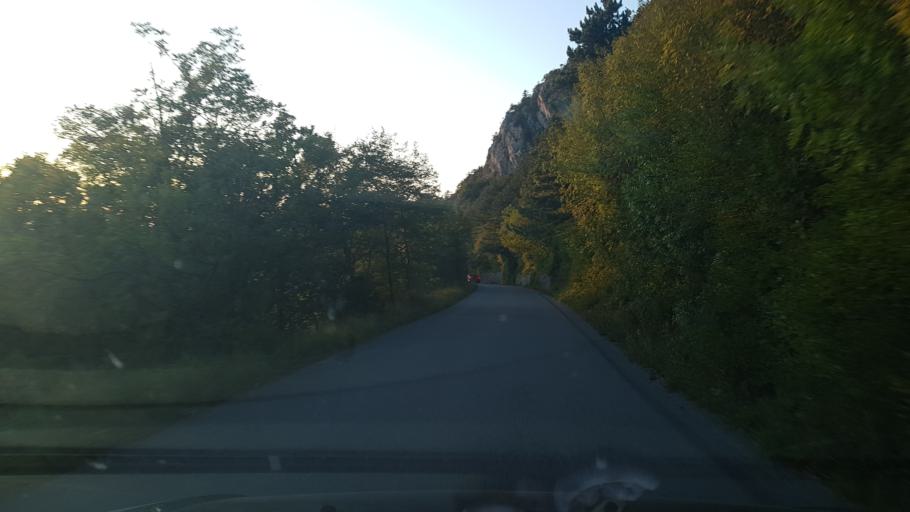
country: SI
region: Vipava
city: Vipava
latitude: 45.7931
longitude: 14.0093
